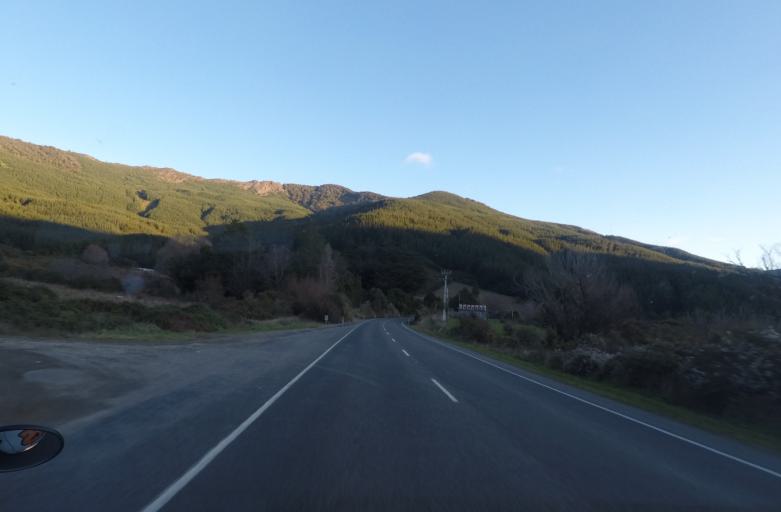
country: NZ
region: Marlborough
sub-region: Marlborough District
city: Picton
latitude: -41.2804
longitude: 173.7275
